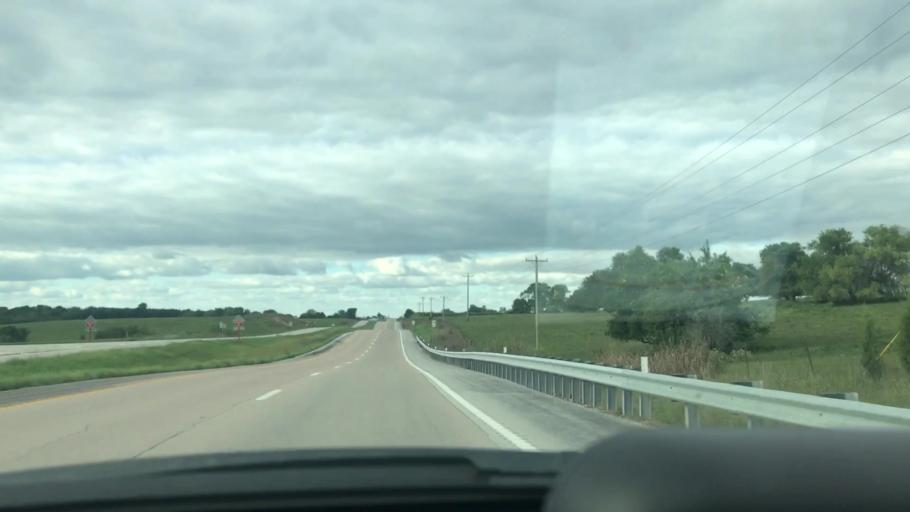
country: US
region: Missouri
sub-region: Benton County
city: Lincoln
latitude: 38.3190
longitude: -93.3423
